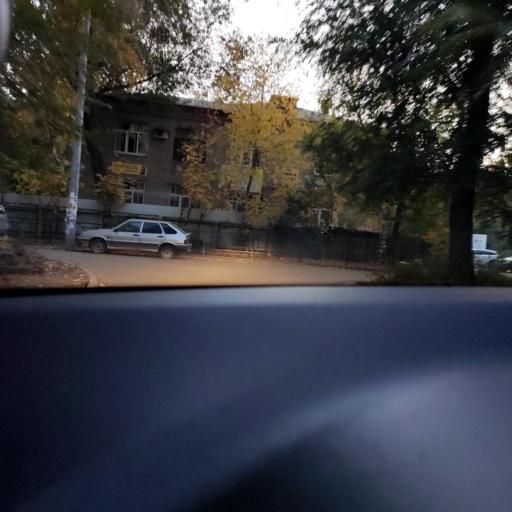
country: RU
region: Samara
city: Samara
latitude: 53.2130
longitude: 50.2566
